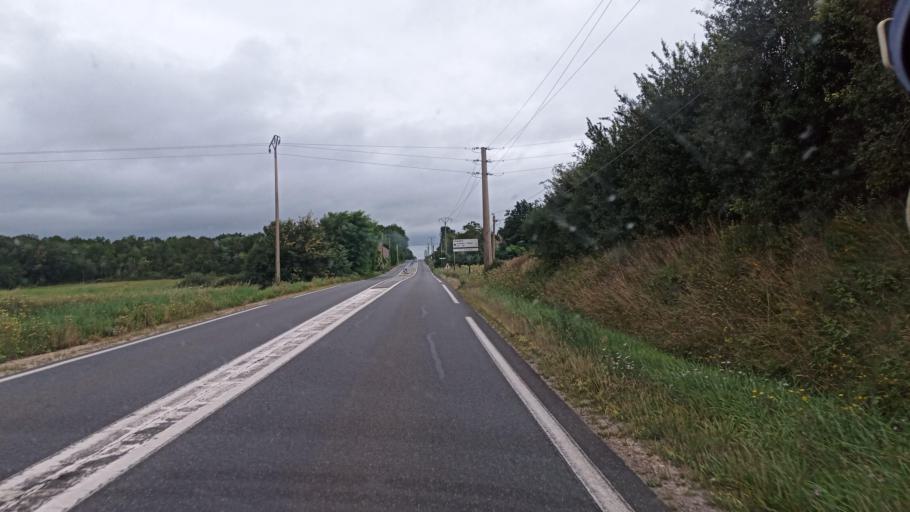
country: FR
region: Ile-de-France
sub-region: Departement de Seine-et-Marne
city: Cannes-Ecluse
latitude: 48.3410
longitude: 2.9580
